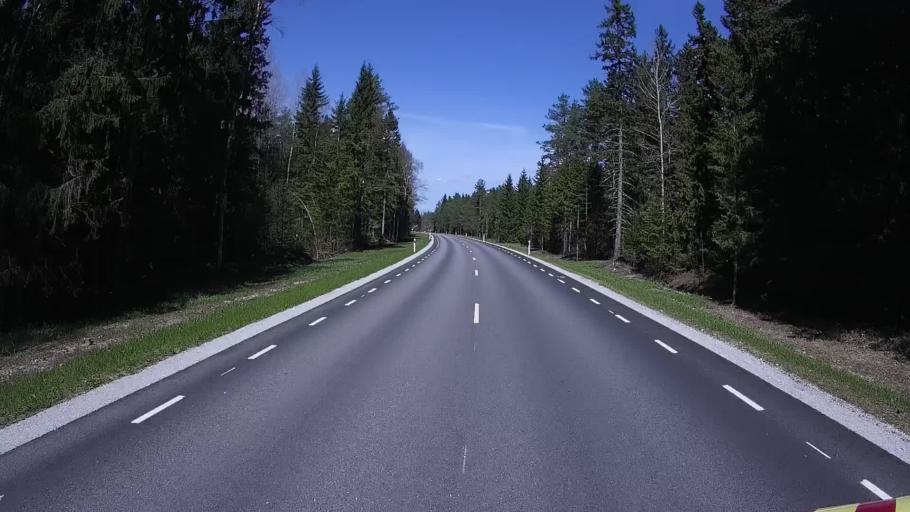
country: EE
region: Harju
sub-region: Nissi vald
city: Turba
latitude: 59.1480
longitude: 24.0782
